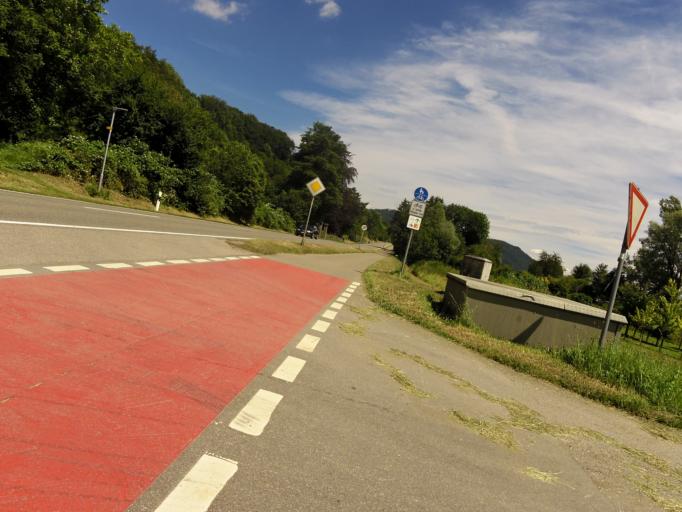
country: DE
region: Baden-Wuerttemberg
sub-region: Freiburg Region
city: Bodman-Ludwigshafen
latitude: 47.8185
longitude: 9.0355
